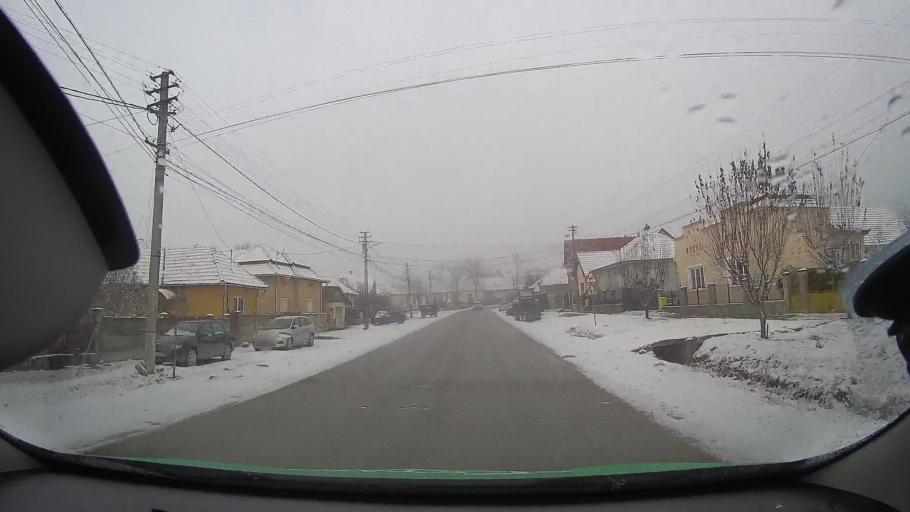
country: RO
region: Alba
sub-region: Municipiul Aiud
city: Ciumbrud
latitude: 46.3061
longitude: 23.7608
